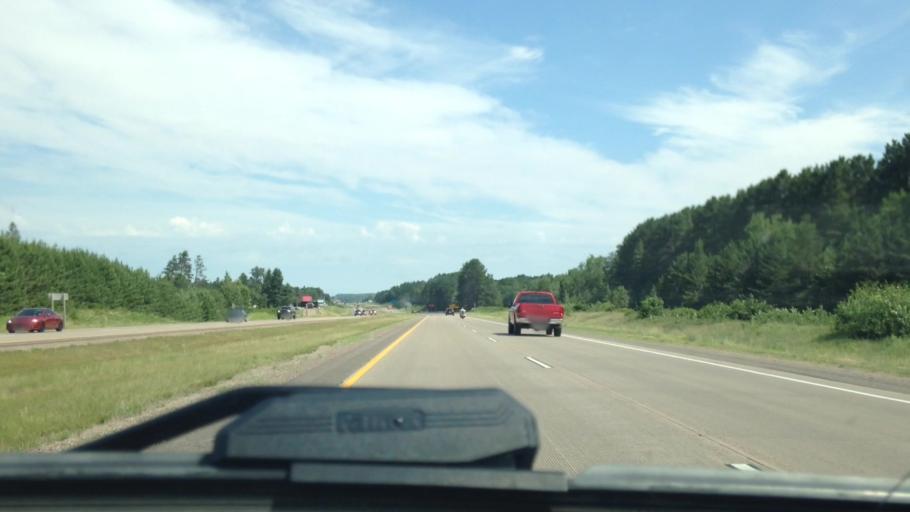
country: US
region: Wisconsin
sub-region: Washburn County
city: Spooner
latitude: 45.8838
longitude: -91.8282
